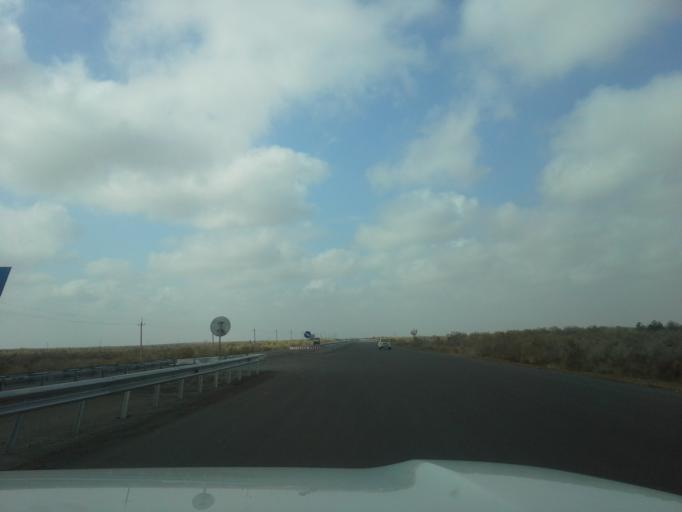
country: TM
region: Mary
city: Mary
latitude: 37.4126
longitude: 61.5451
